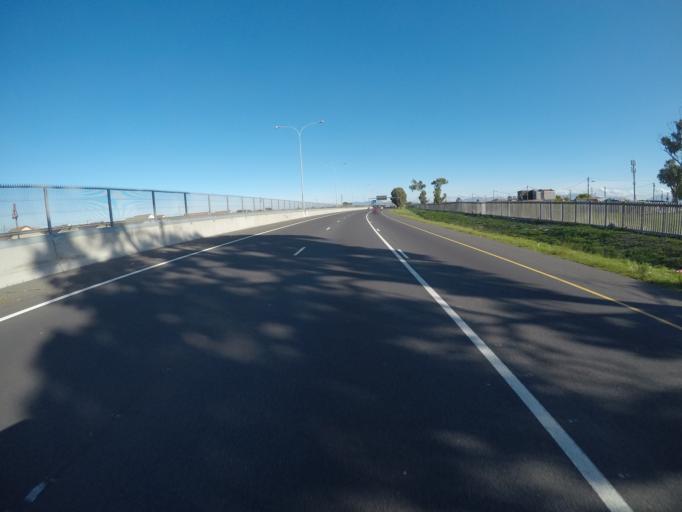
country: ZA
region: Western Cape
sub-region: City of Cape Town
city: Kraaifontein
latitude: -33.9838
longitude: 18.6507
